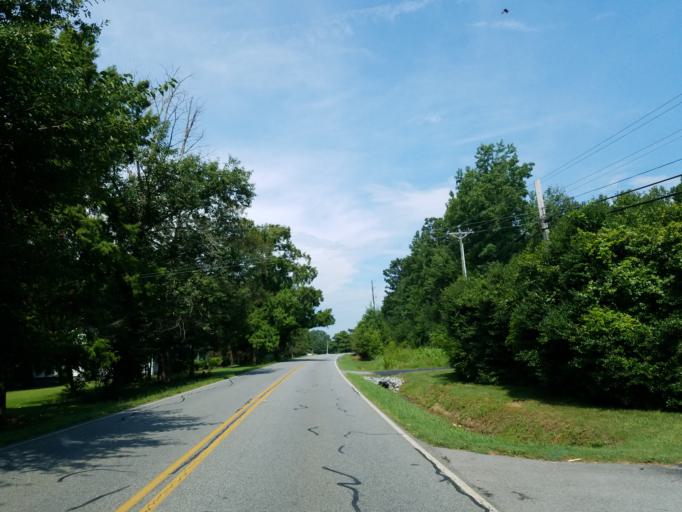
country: US
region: Georgia
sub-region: Gordon County
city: Calhoun
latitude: 34.5272
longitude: -84.8680
